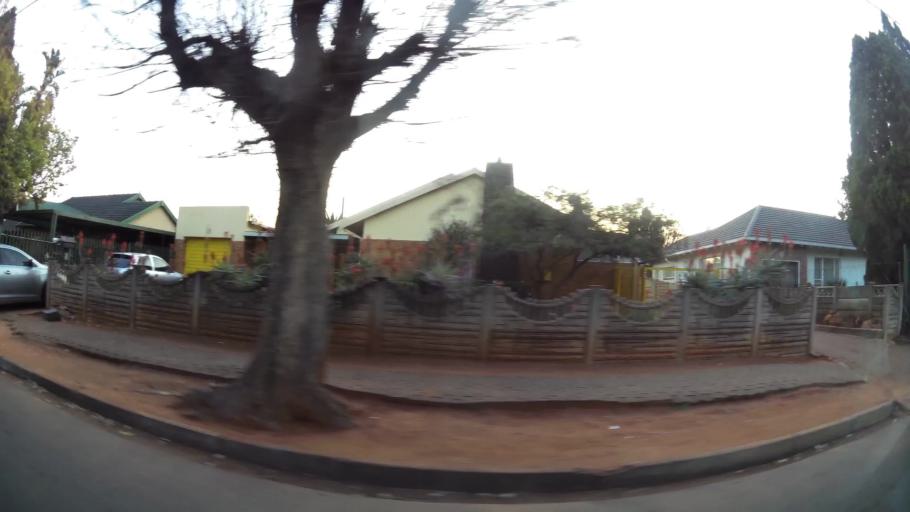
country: ZA
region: Gauteng
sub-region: Ekurhuleni Metropolitan Municipality
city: Tembisa
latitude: -26.0625
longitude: 28.2305
